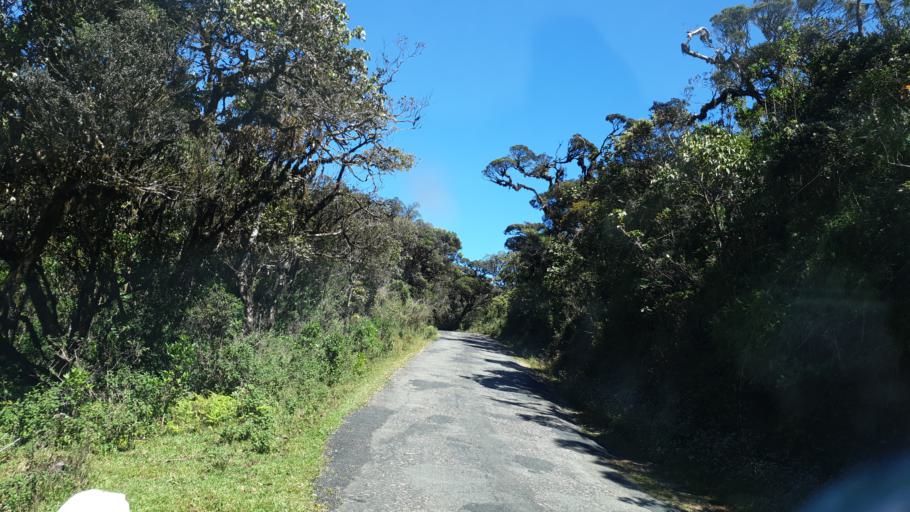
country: LK
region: Central
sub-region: Nuwara Eliya District
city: Nuwara Eliya
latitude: 6.8315
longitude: 80.8073
